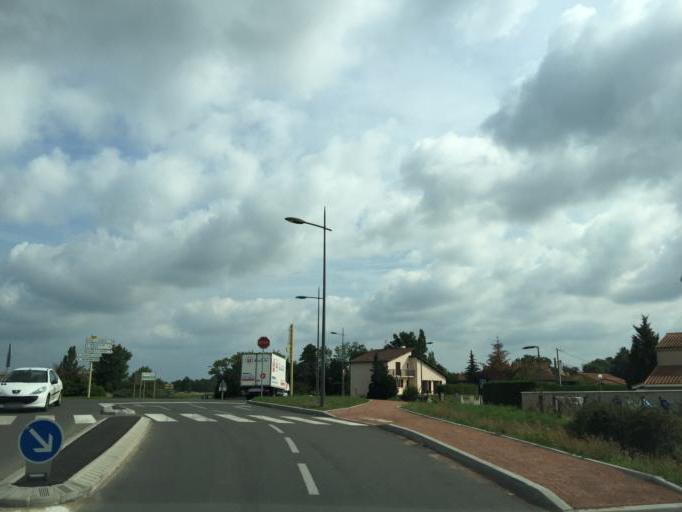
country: FR
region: Rhone-Alpes
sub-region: Departement de la Loire
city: Saint-Romain-le-Puy
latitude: 45.5516
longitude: 4.1258
